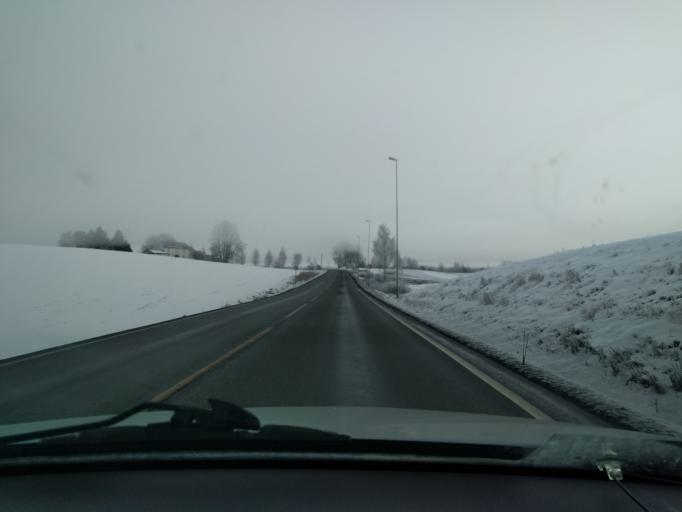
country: NO
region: Hedmark
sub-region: Loten
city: Loten
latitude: 60.8412
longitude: 11.3450
